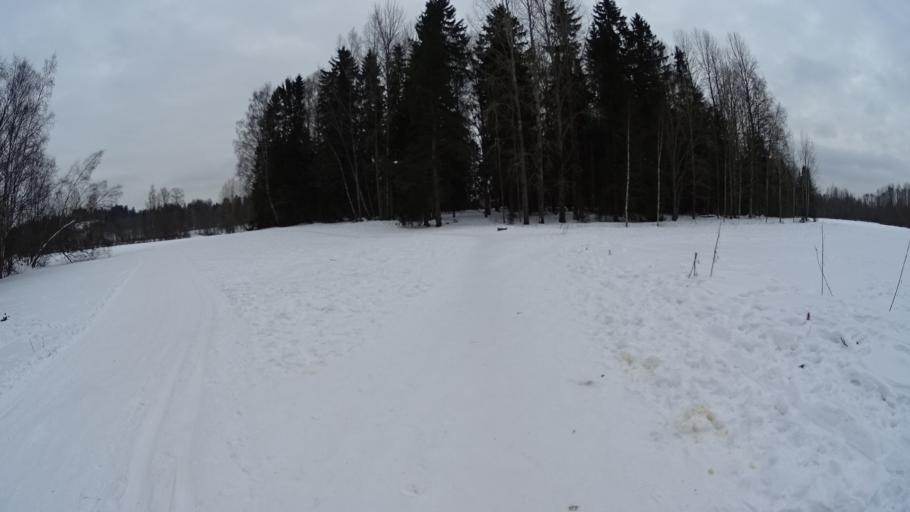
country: FI
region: Uusimaa
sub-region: Helsinki
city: Kauniainen
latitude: 60.2466
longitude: 24.7306
